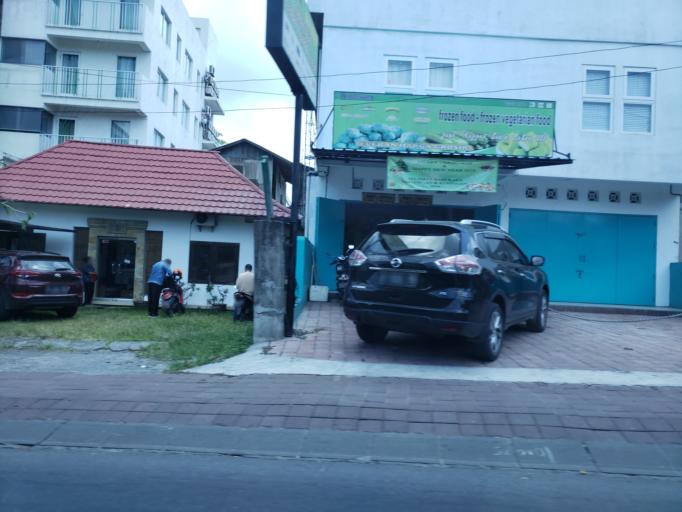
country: ID
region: Bali
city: Jimbaran
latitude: -8.8127
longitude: 115.1573
